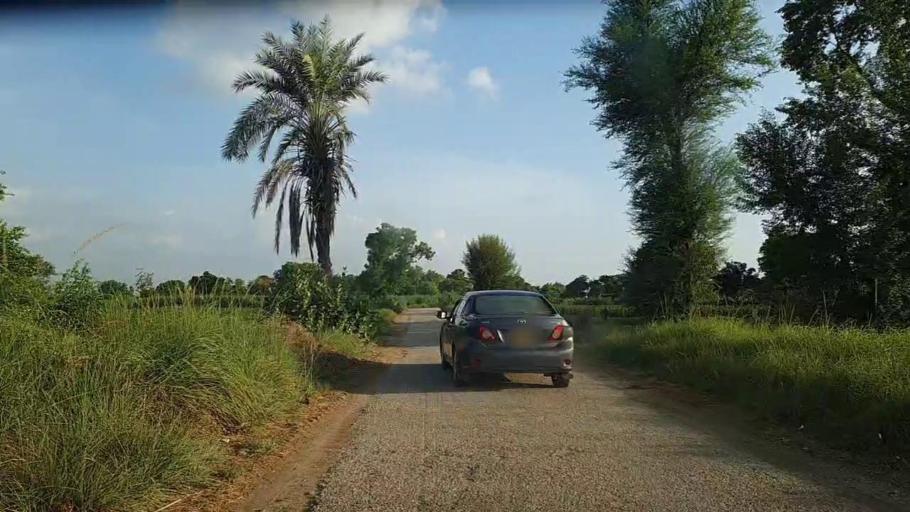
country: PK
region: Sindh
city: Hingorja
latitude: 27.0619
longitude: 68.4188
